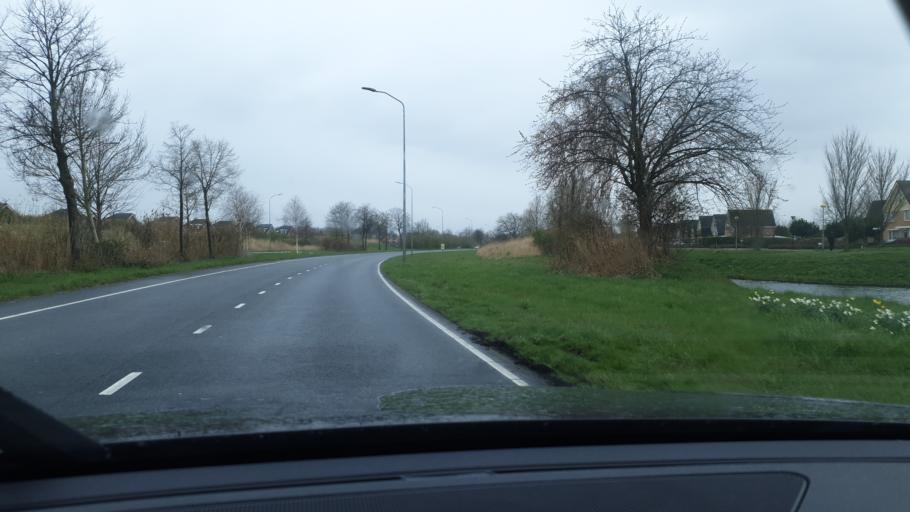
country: NL
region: Flevoland
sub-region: Gemeente Lelystad
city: Lelystad
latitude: 52.4925
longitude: 5.5090
